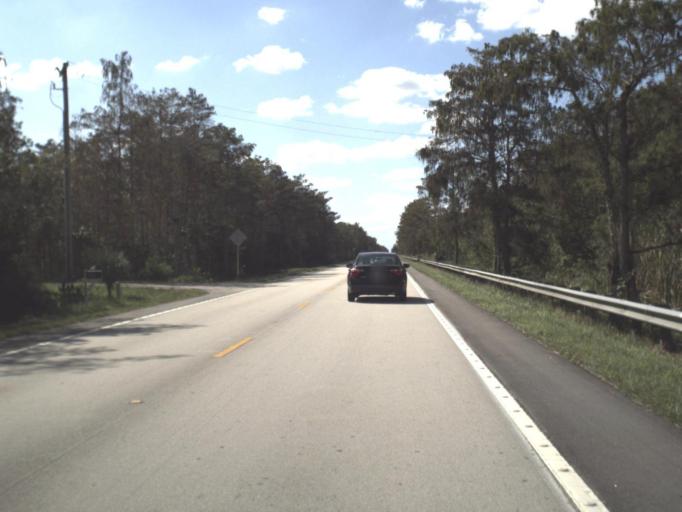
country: US
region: Florida
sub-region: Miami-Dade County
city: Kendall West
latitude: 25.8560
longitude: -81.0244
